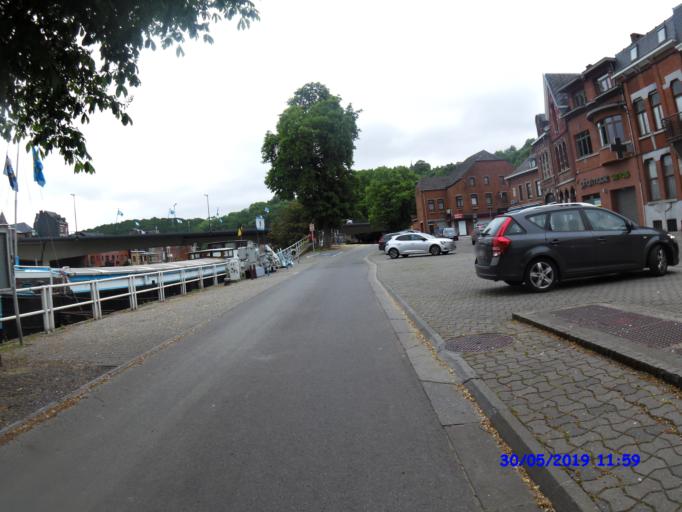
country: BE
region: Wallonia
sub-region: Province du Hainaut
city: Thuin
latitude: 50.3414
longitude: 4.2859
